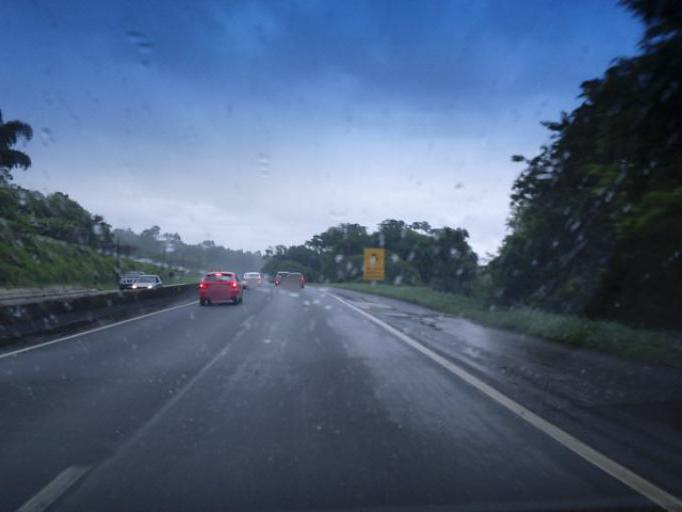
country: BR
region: Santa Catarina
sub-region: Barra Velha
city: Barra Velha
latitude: -26.6999
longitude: -48.6989
